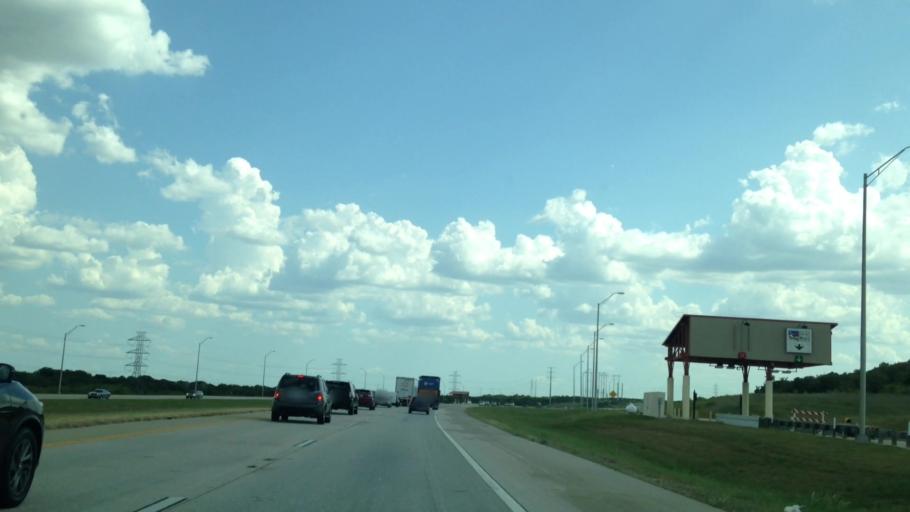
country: US
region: Texas
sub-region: Travis County
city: Manor
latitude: 30.3072
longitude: -97.5708
